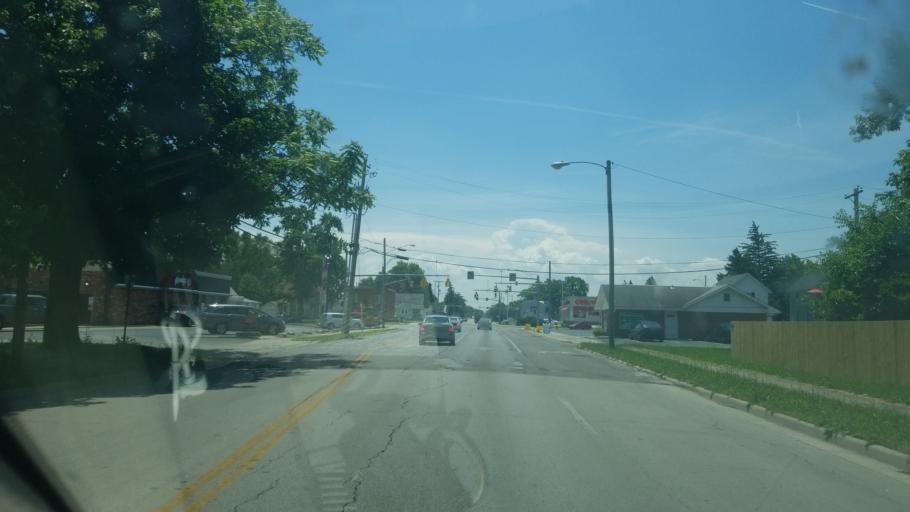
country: US
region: Ohio
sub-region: Hancock County
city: Findlay
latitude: 41.0465
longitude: -83.6414
